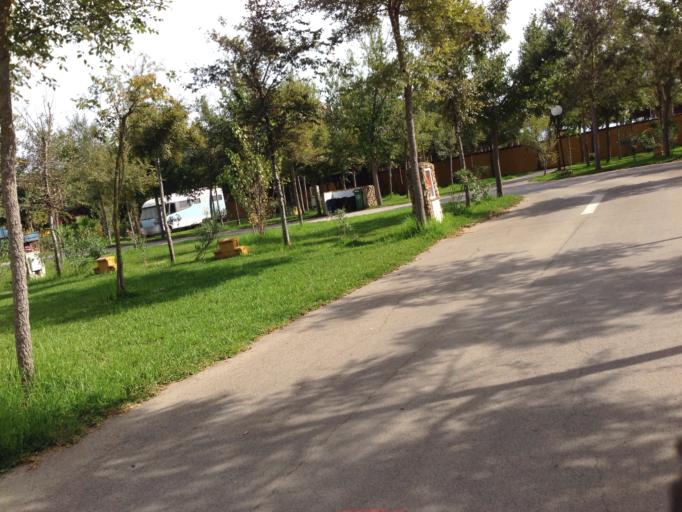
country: ES
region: Andalusia
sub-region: Provincia de Cadiz
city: Conil de la Frontera
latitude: 36.3113
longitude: -6.1134
